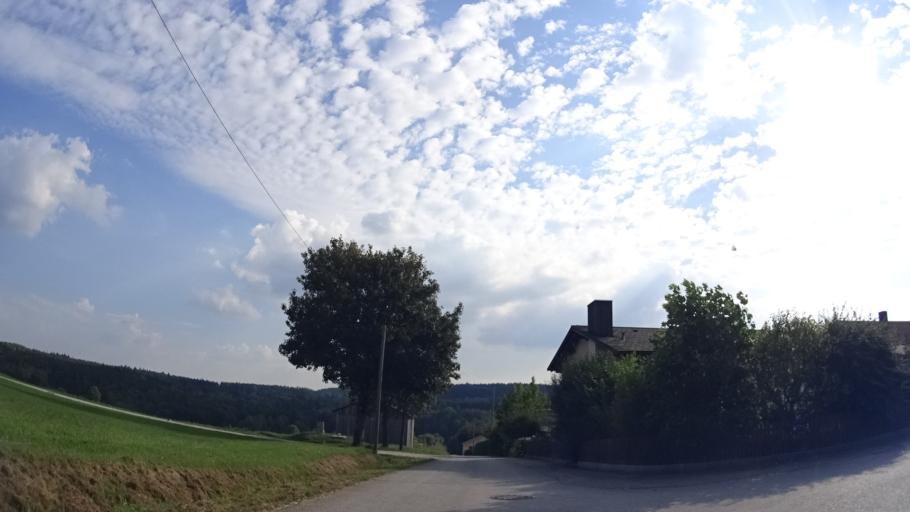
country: DE
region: Bavaria
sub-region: Lower Bavaria
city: Riedenburg
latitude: 48.9335
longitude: 11.6465
